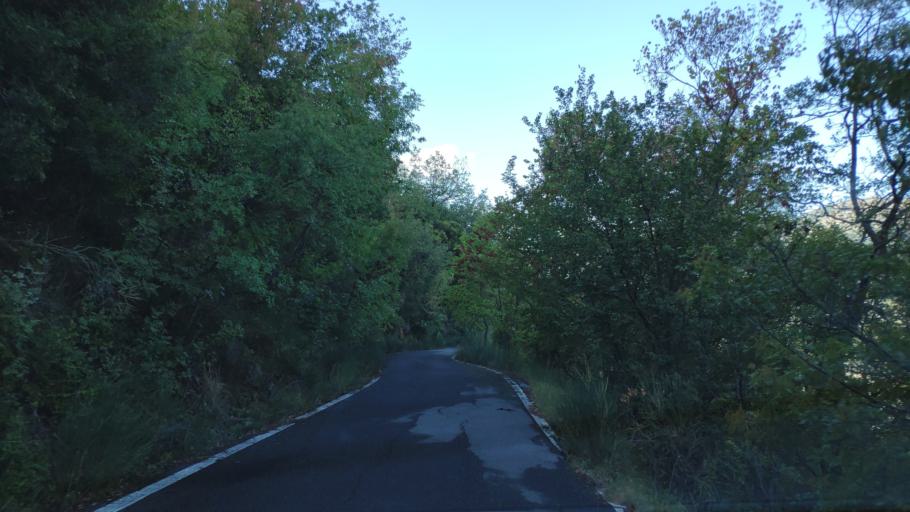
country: GR
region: Peloponnese
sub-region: Nomos Arkadias
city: Dimitsana
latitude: 37.5498
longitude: 22.0459
